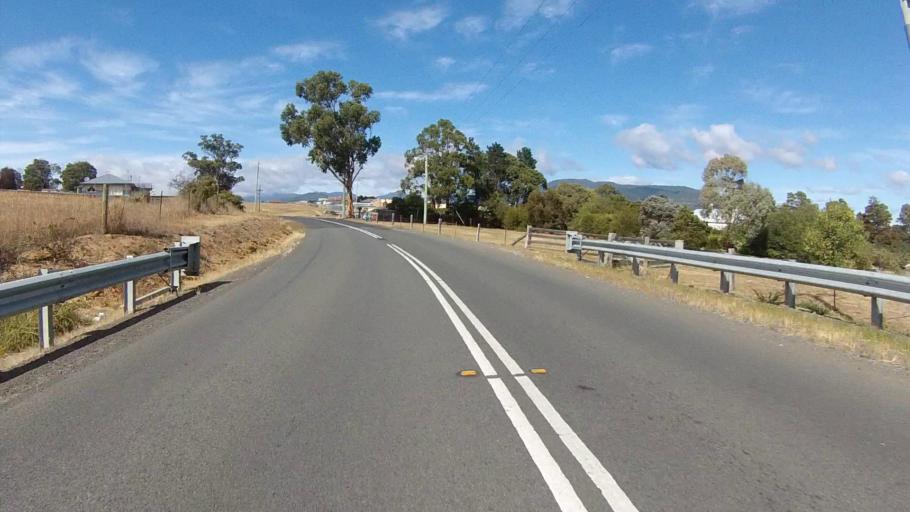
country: AU
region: Tasmania
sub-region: Brighton
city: Old Beach
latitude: -42.7455
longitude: 147.2817
